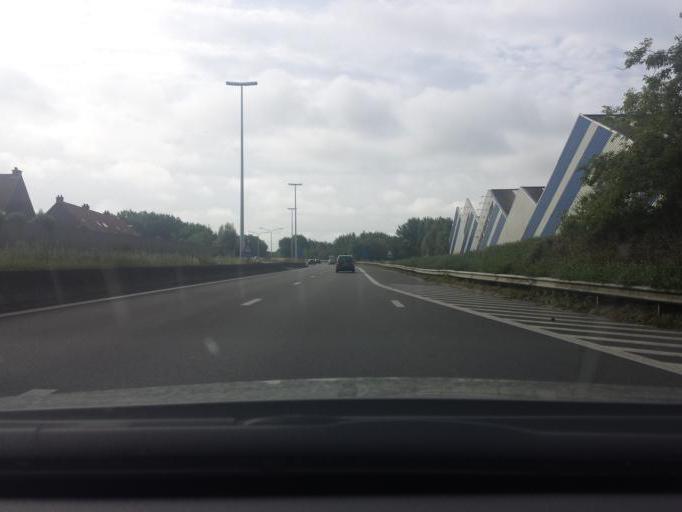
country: BE
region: Flanders
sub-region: Provincie West-Vlaanderen
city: Kortrijk
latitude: 50.8182
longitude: 3.2288
